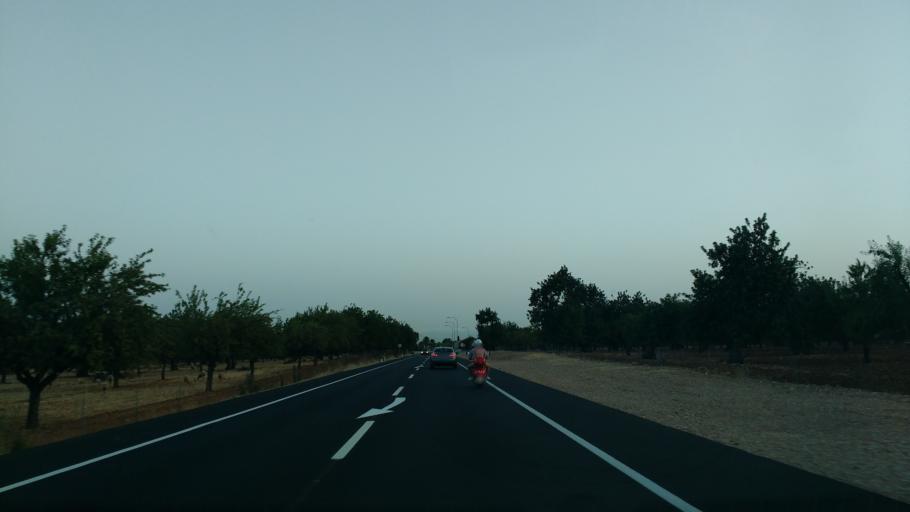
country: ES
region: Balearic Islands
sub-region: Illes Balears
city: Bunyola
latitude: 39.6715
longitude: 2.6778
